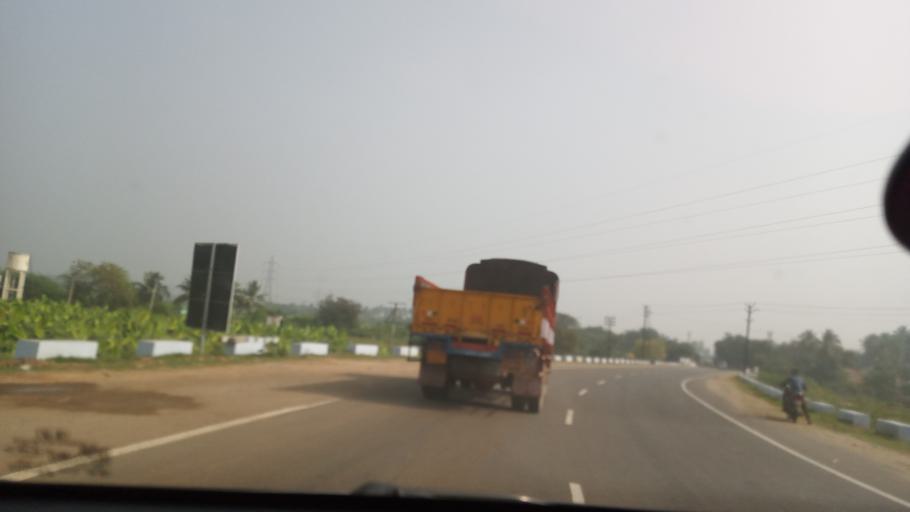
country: IN
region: Tamil Nadu
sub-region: Erode
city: Sathyamangalam
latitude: 11.4500
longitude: 77.2133
